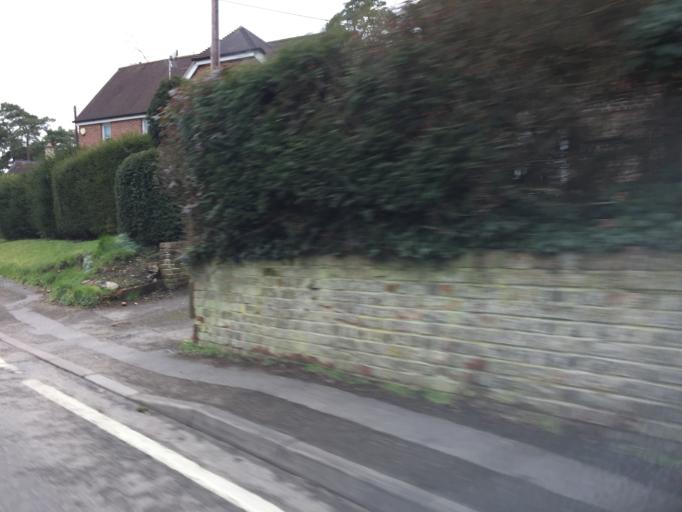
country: GB
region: England
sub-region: West Berkshire
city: Basildon
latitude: 51.5050
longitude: -1.1236
